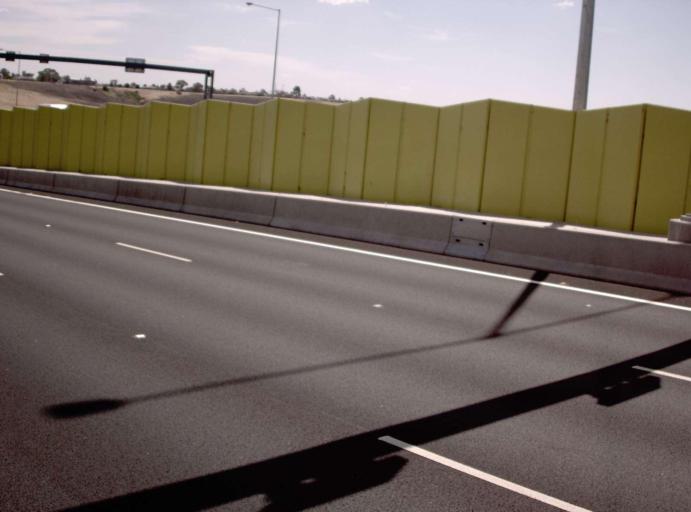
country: AU
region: Victoria
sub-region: Hume
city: Jacana
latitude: -37.6940
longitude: 144.9107
